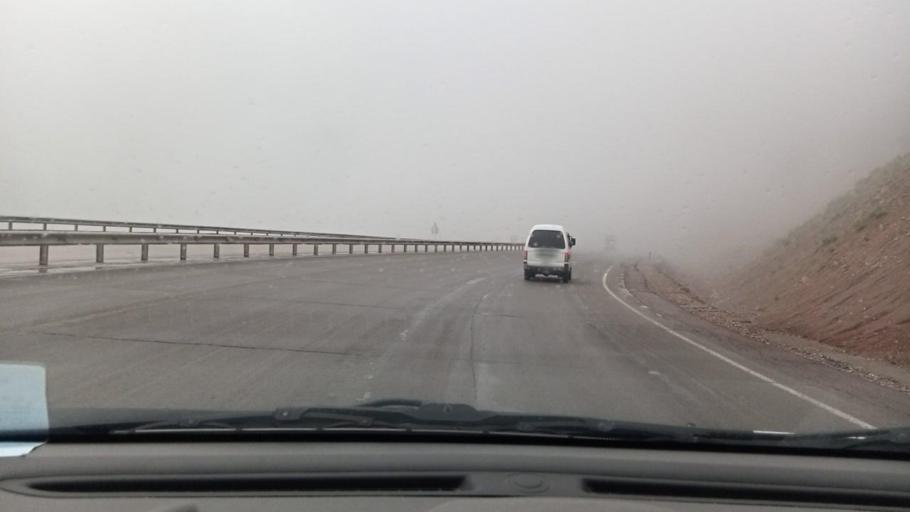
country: UZ
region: Toshkent
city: Angren
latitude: 41.1081
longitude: 70.5074
